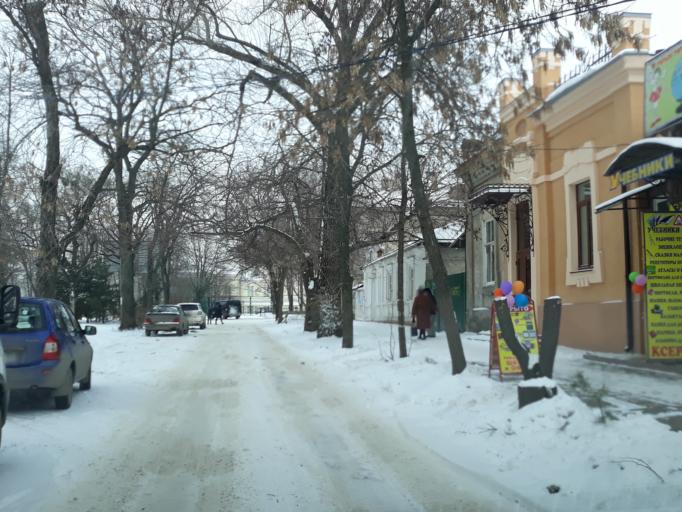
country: RU
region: Rostov
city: Taganrog
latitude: 47.2137
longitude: 38.9204
